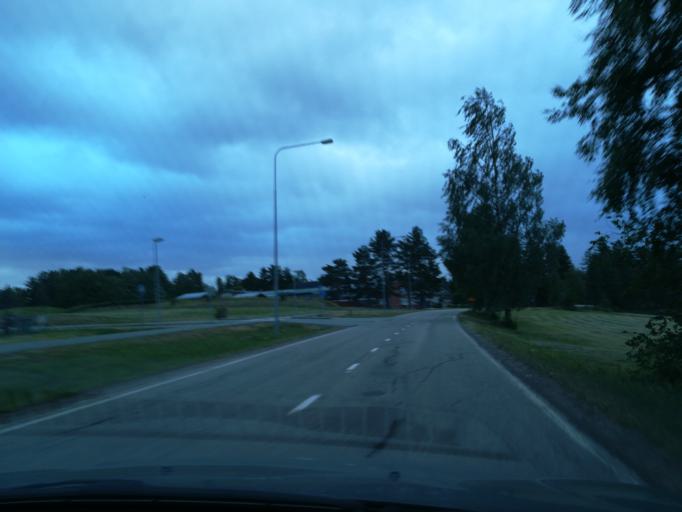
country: FI
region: Southern Savonia
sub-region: Mikkeli
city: Ristiina
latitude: 61.5045
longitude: 27.2648
